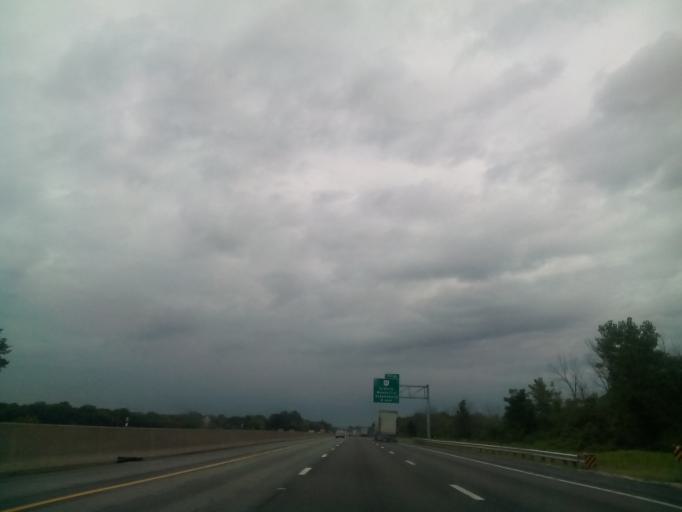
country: US
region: Ohio
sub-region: Ottawa County
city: Elmore
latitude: 41.4700
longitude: -83.3190
